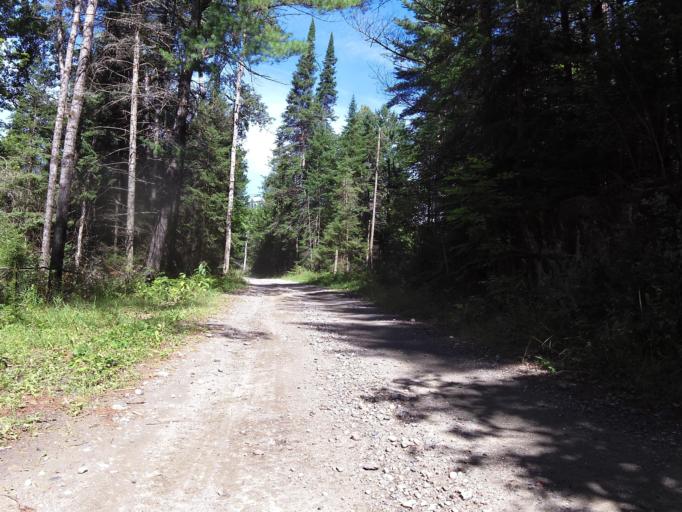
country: CA
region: Ontario
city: Renfrew
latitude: 45.0793
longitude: -76.7200
